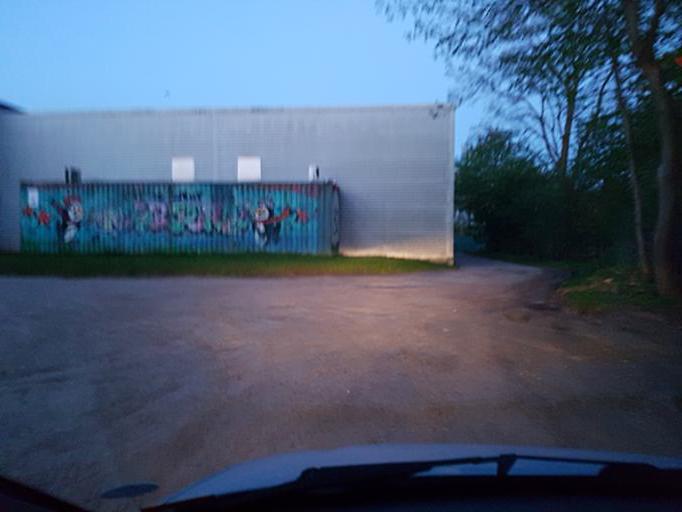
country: DK
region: South Denmark
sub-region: Esbjerg Kommune
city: Esbjerg
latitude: 55.4823
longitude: 8.4352
